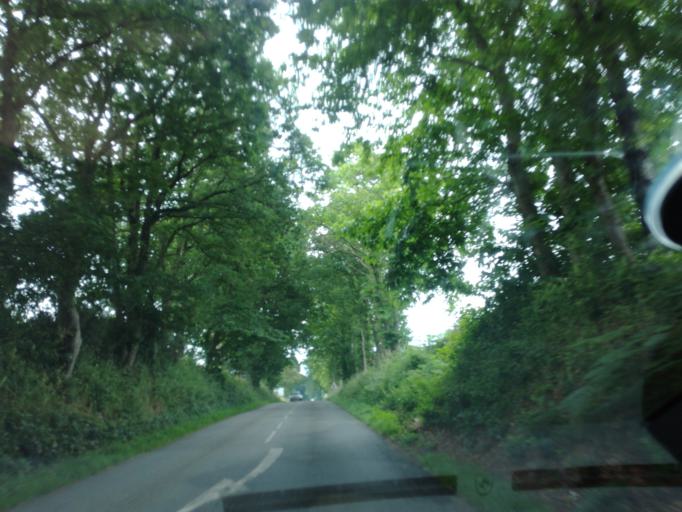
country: FR
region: Brittany
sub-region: Departement du Morbihan
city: Saint-Thuriau
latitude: 48.0323
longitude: -2.9643
